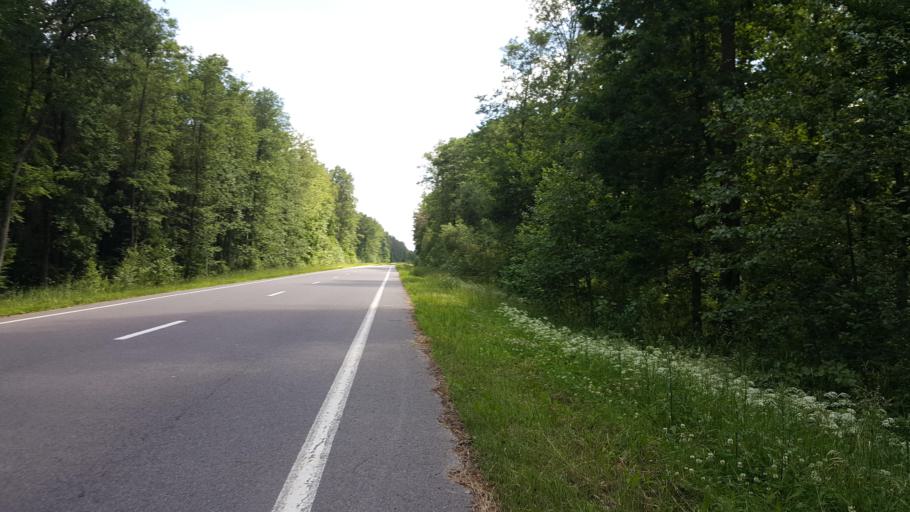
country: BY
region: Brest
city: Kamyanyuki
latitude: 52.5416
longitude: 23.6537
